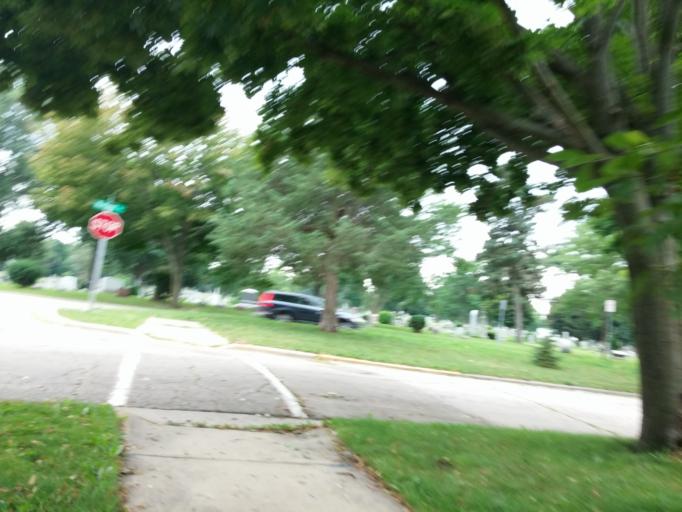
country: US
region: Wisconsin
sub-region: Dane County
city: Shorewood Hills
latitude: 43.0683
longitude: -89.4315
